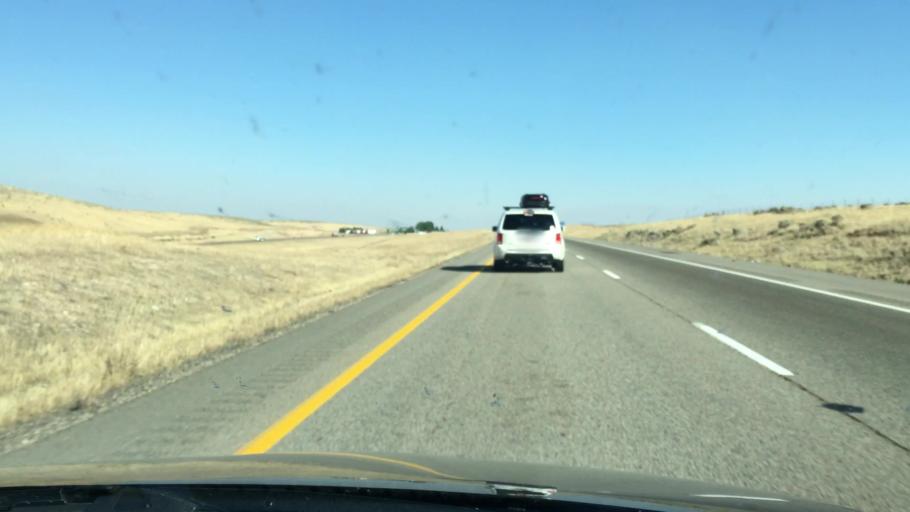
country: US
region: Idaho
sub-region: Ada County
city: Boise
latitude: 43.4852
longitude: -116.1182
